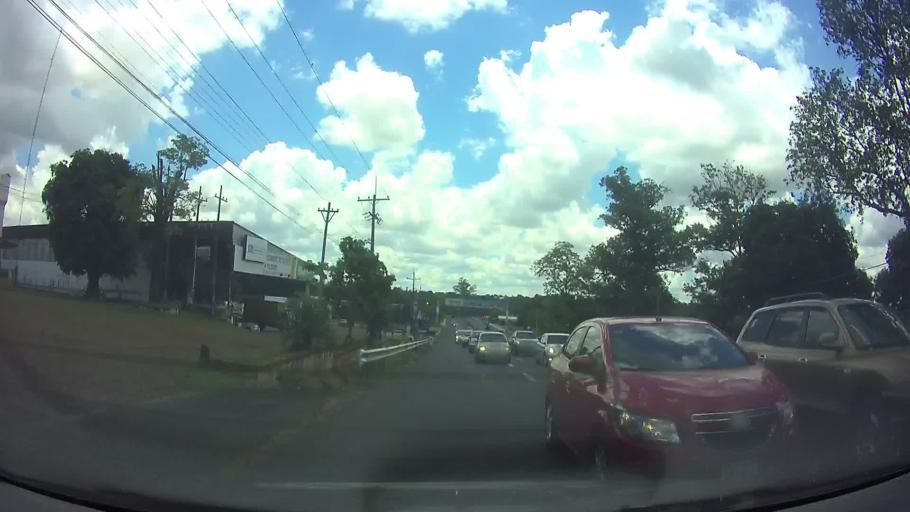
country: PY
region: Central
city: Capiata
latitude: -25.3778
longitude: -57.3997
